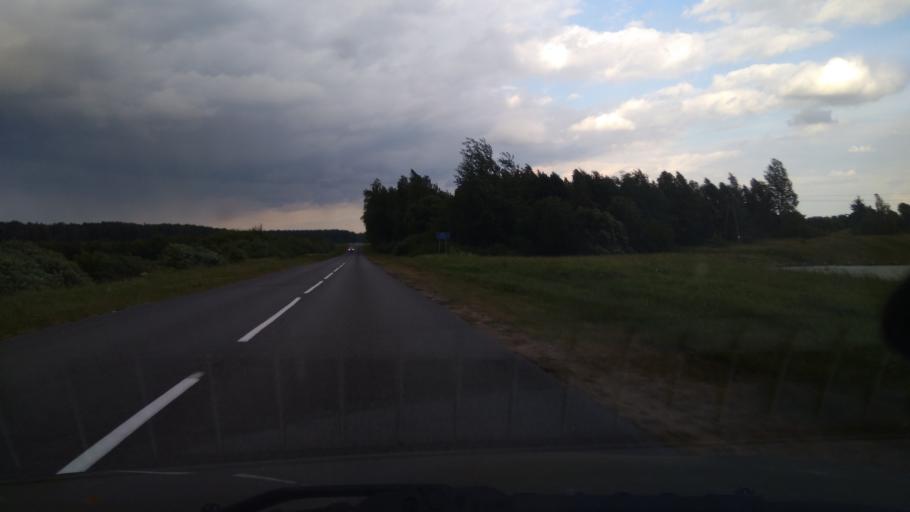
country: BY
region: Minsk
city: Il'ya
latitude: 54.4283
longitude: 27.1963
